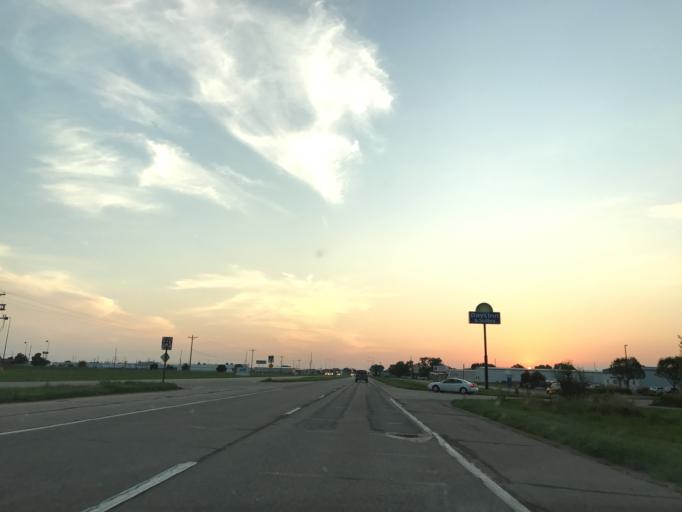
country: US
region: Nebraska
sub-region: Platte County
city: Columbus
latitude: 41.4385
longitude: -97.3046
